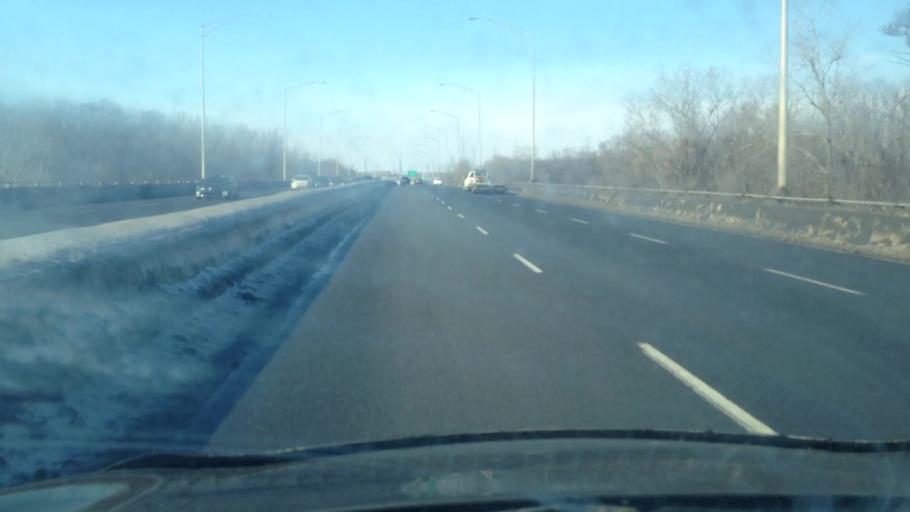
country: CA
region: Quebec
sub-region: Laurentides
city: Boisbriand
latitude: 45.5796
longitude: -73.8363
